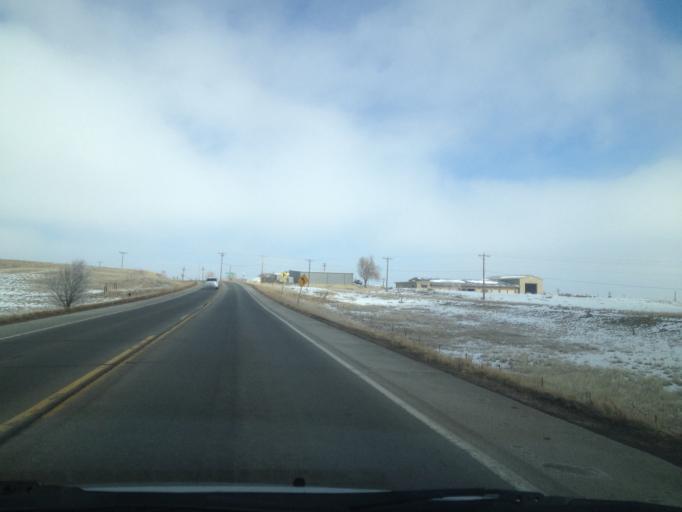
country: US
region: Colorado
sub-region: Boulder County
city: Boulder
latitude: 40.0776
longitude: -105.2832
